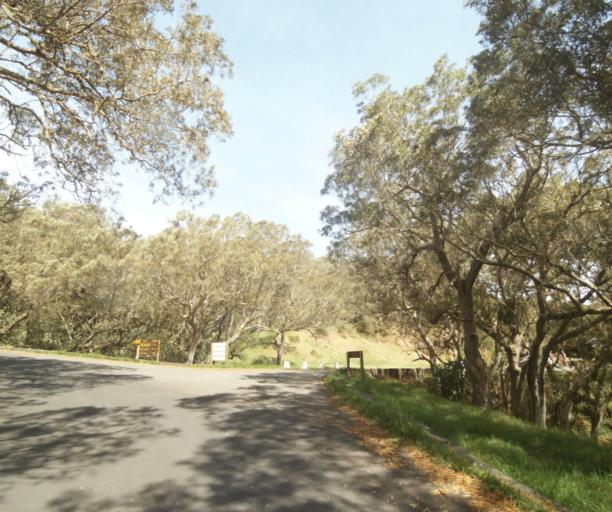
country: RE
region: Reunion
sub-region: Reunion
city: Trois-Bassins
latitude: -21.0593
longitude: 55.3663
